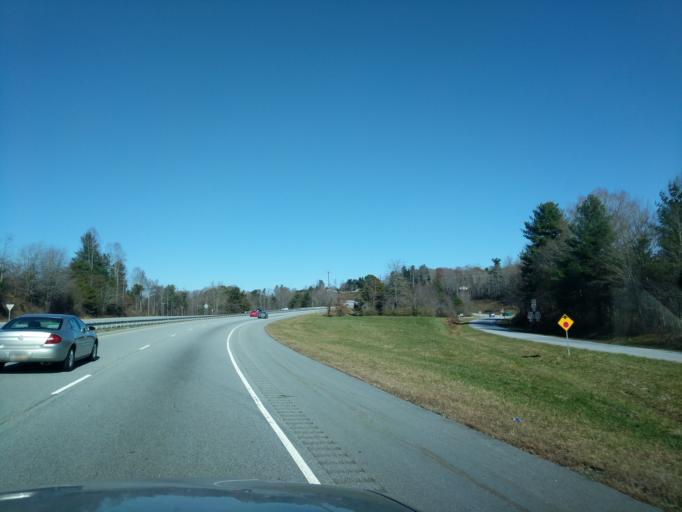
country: US
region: North Carolina
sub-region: Henderson County
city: East Flat Rock
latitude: 35.2562
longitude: -82.4093
